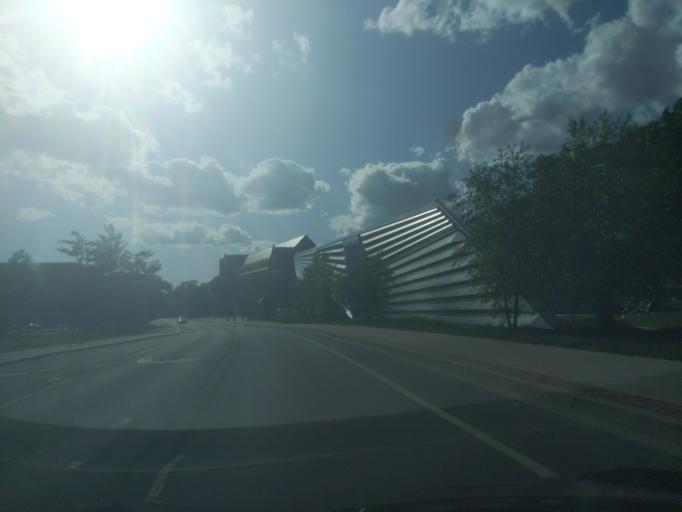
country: US
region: Michigan
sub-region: Ingham County
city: East Lansing
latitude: 42.7324
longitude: -84.4758
